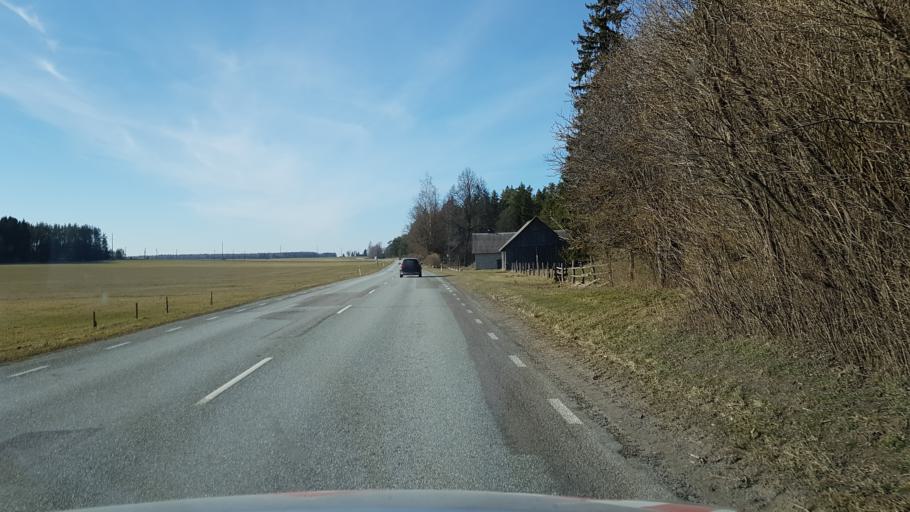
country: EE
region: Laeaene-Virumaa
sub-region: Vinni vald
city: Vinni
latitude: 59.1889
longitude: 26.5734
